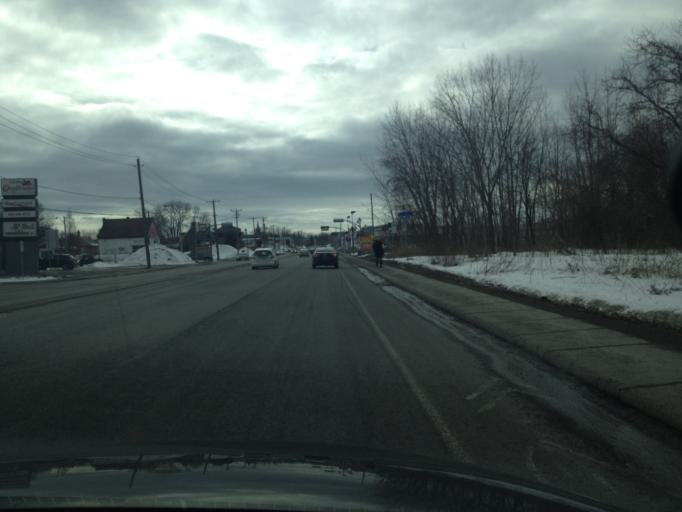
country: CA
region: Quebec
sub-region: Laval
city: Laval
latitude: 45.5547
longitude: -73.7535
